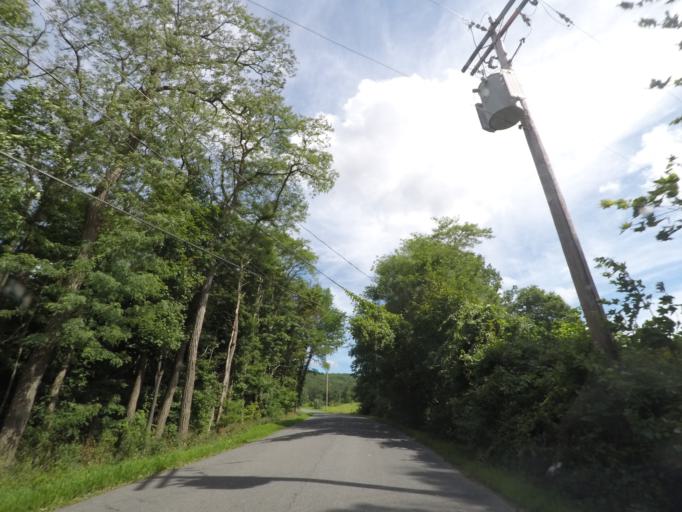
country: US
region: New York
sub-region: Rensselaer County
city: Poestenkill
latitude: 42.6870
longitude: -73.5605
